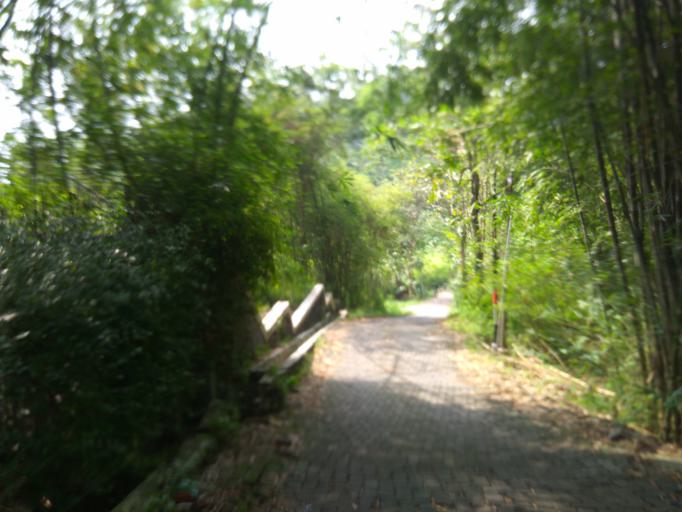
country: ID
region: Central Java
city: Semarang
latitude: -7.0327
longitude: 110.4073
